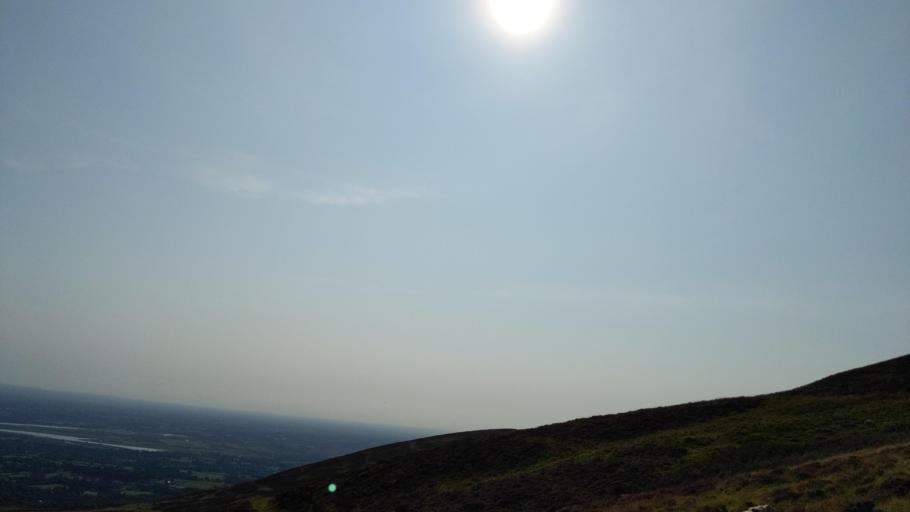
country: GB
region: Northern Ireland
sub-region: Down District
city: Warrenpoint
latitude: 54.0752
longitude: -6.3188
